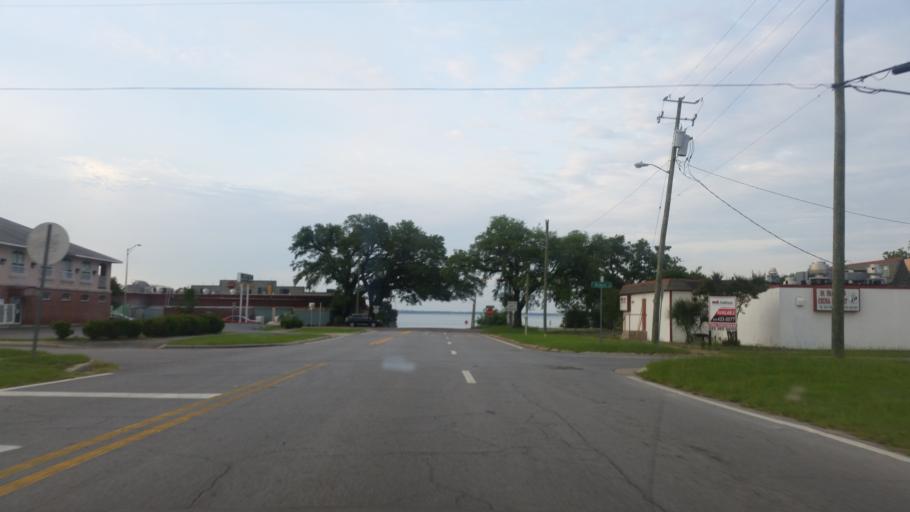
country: US
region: Florida
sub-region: Escambia County
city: Pensacola
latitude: 30.4193
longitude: -87.1986
